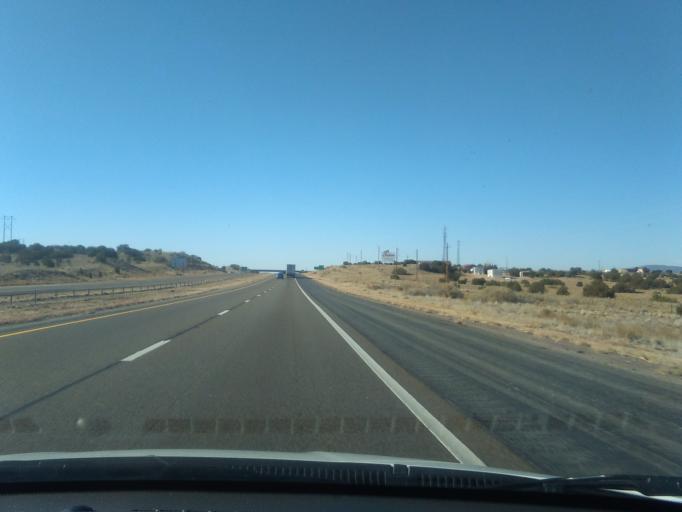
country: US
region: New Mexico
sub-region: Sandoval County
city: Santo Domingo Pueblo
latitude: 35.4629
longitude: -106.3227
